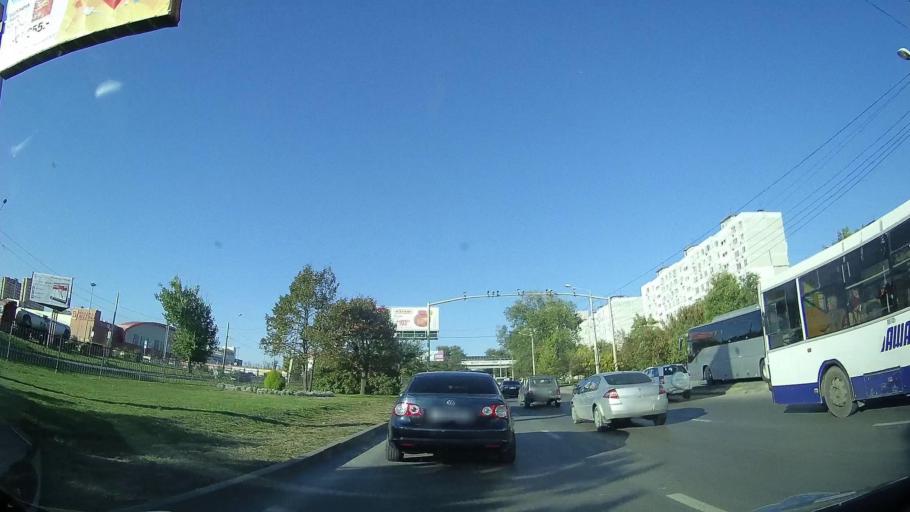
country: RU
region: Rostov
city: Kalinin
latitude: 47.2277
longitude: 39.6140
